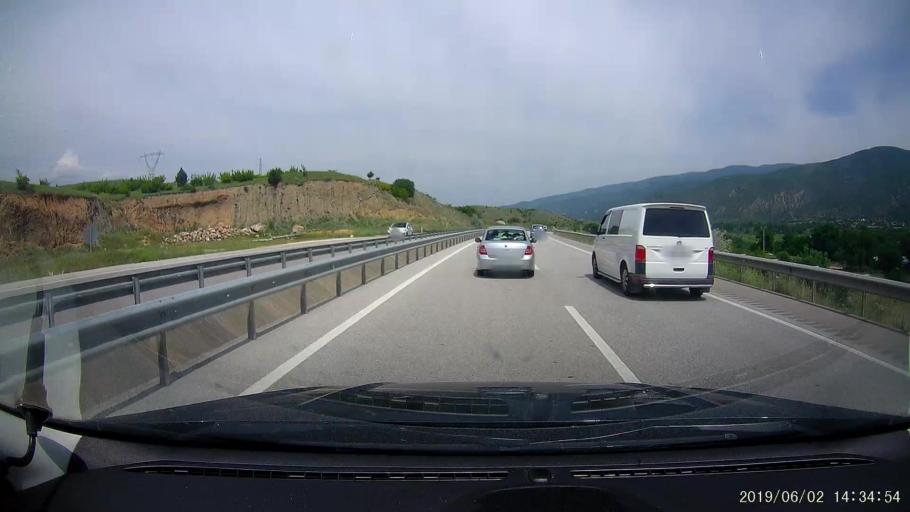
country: TR
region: Kastamonu
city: Tosya
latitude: 41.0407
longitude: 34.2028
